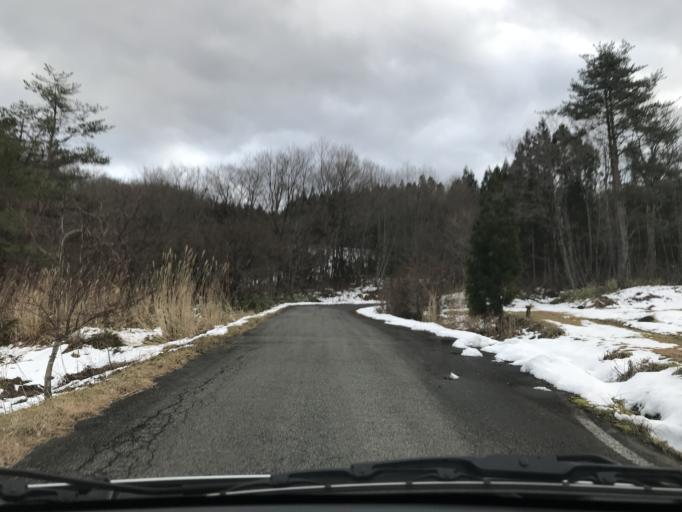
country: JP
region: Iwate
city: Ichinoseki
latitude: 38.9959
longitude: 140.9983
